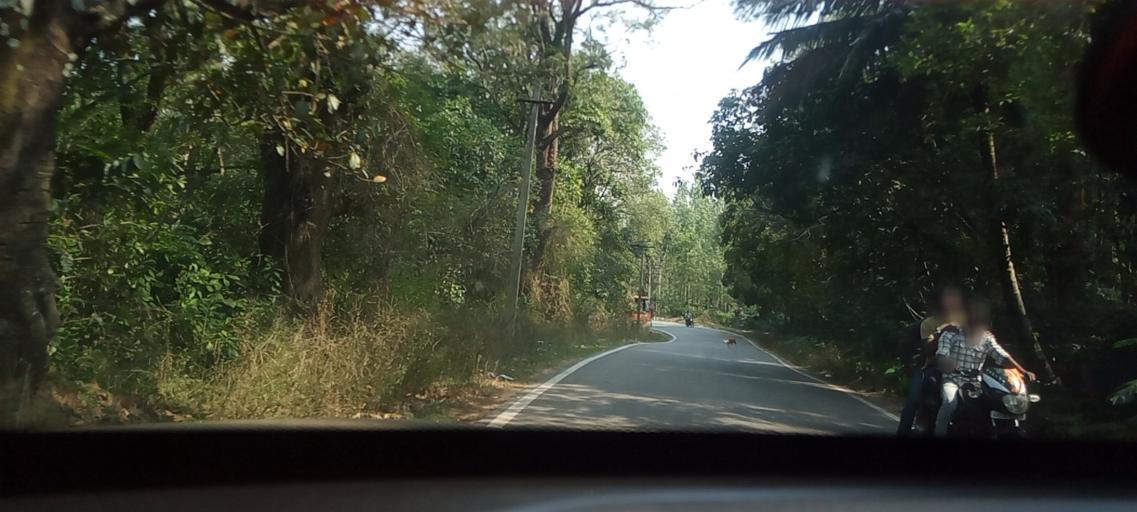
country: IN
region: Karnataka
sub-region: Hassan
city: Belur
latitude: 13.1888
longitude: 75.7935
